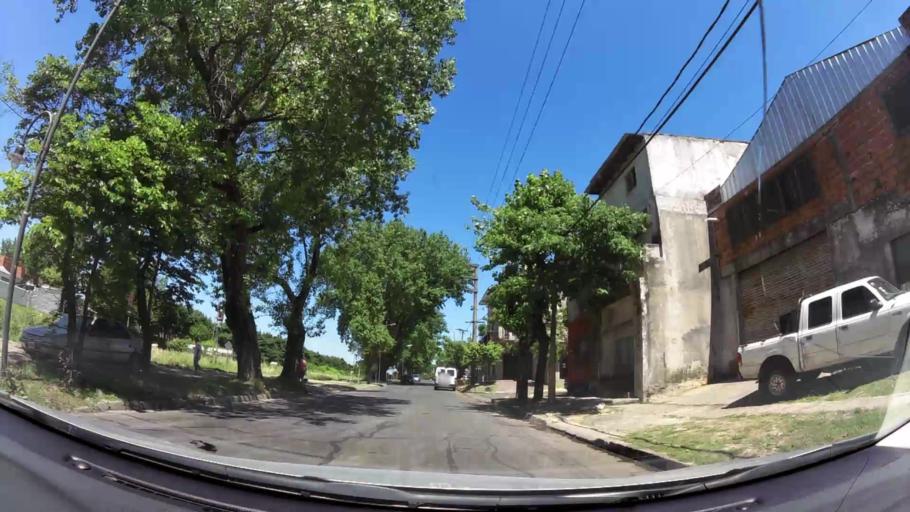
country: AR
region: Buenos Aires
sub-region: Partido de Tigre
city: Tigre
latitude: -34.4627
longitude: -58.5556
